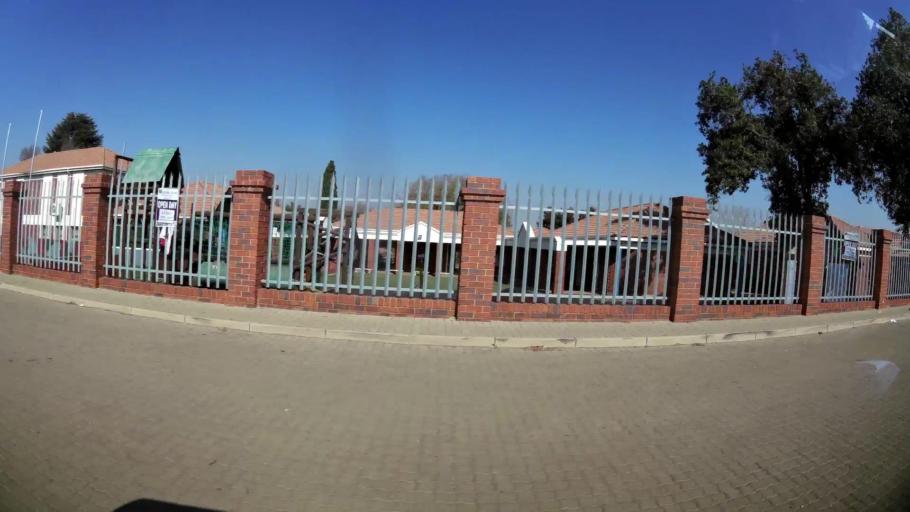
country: ZA
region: Gauteng
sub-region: Ekurhuleni Metropolitan Municipality
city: Boksburg
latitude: -26.1692
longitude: 28.2564
